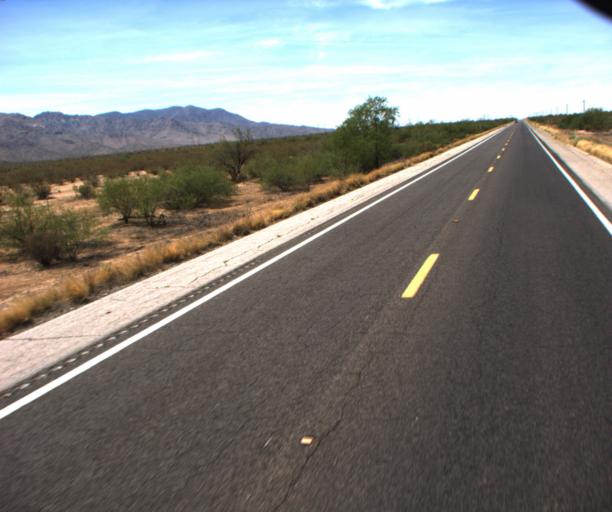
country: US
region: Arizona
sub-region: La Paz County
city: Salome
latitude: 33.9148
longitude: -113.2643
